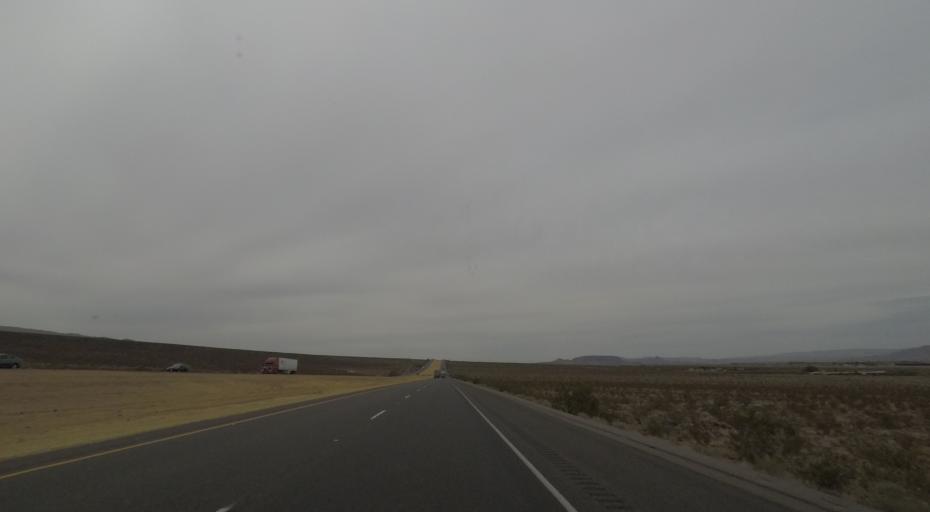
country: US
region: California
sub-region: San Bernardino County
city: Barstow
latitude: 34.8375
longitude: -116.7729
